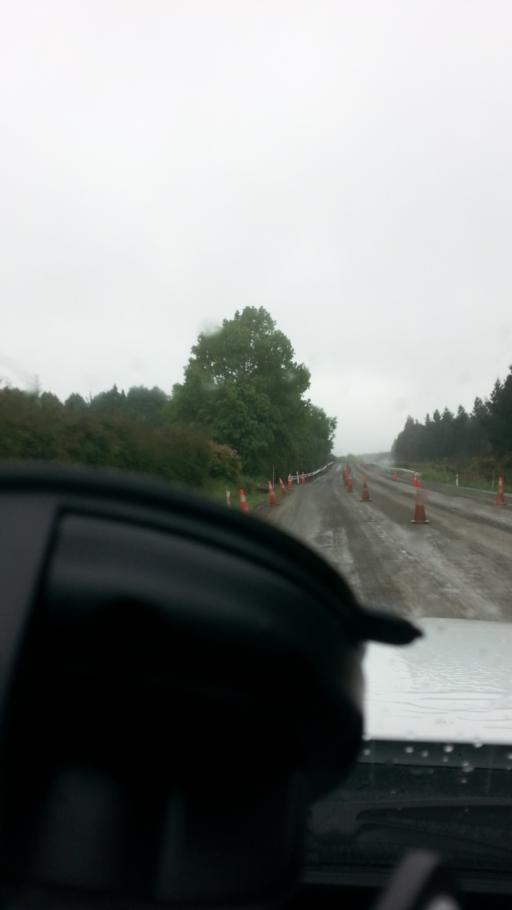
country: NZ
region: Wellington
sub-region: Masterton District
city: Masterton
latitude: -40.8091
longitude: 175.6203
